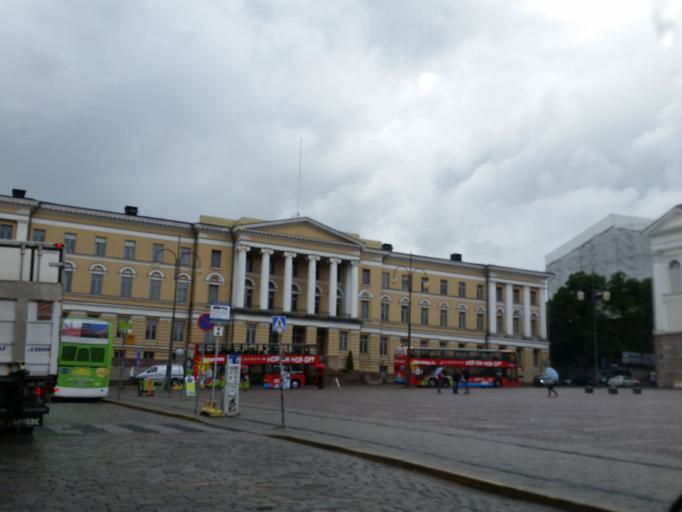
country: FI
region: Uusimaa
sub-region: Helsinki
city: Helsinki
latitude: 60.1691
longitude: 24.9523
